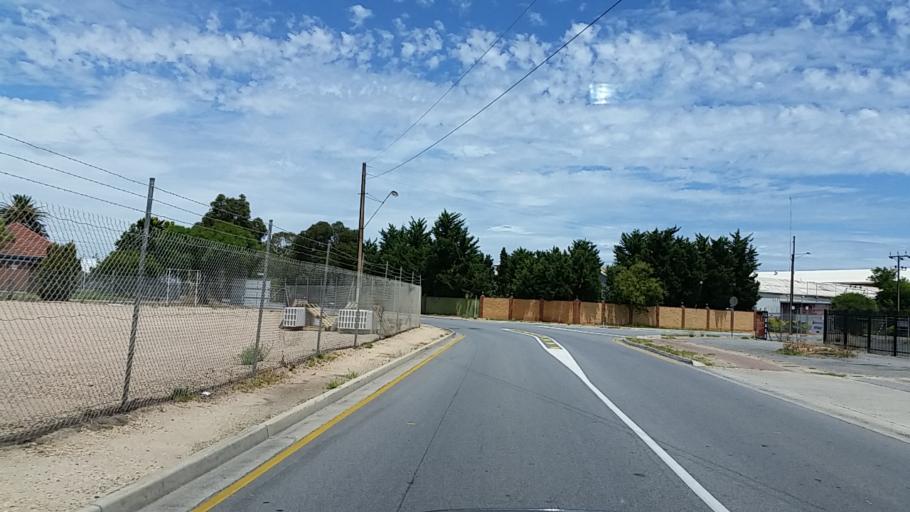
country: AU
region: South Australia
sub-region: Charles Sturt
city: Woodville North
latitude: -34.8651
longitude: 138.5384
